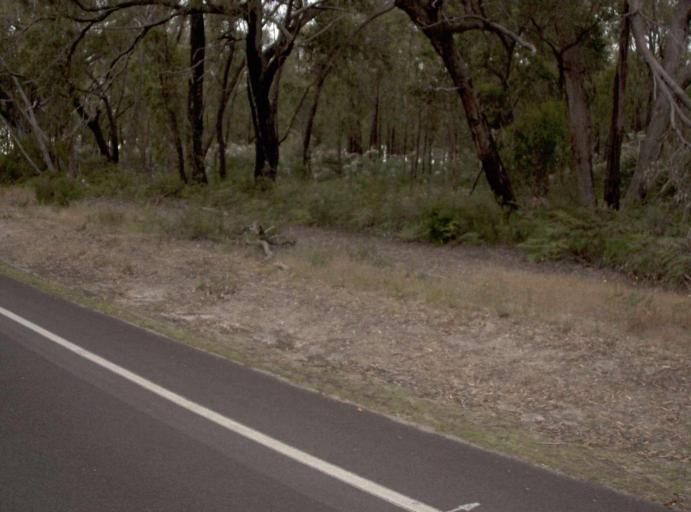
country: AU
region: Victoria
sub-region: Wellington
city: Sale
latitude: -38.3172
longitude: 147.0246
